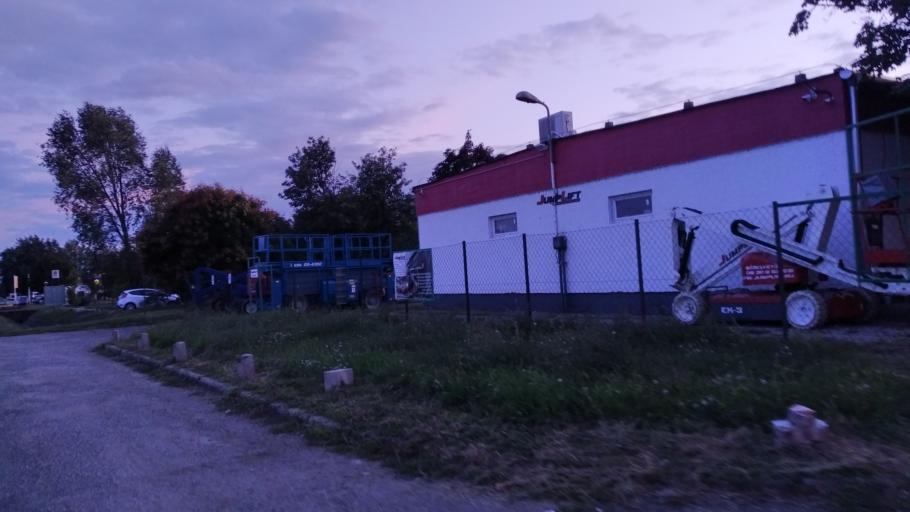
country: HU
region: Pest
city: Budakalasz
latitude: 47.6224
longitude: 19.0638
